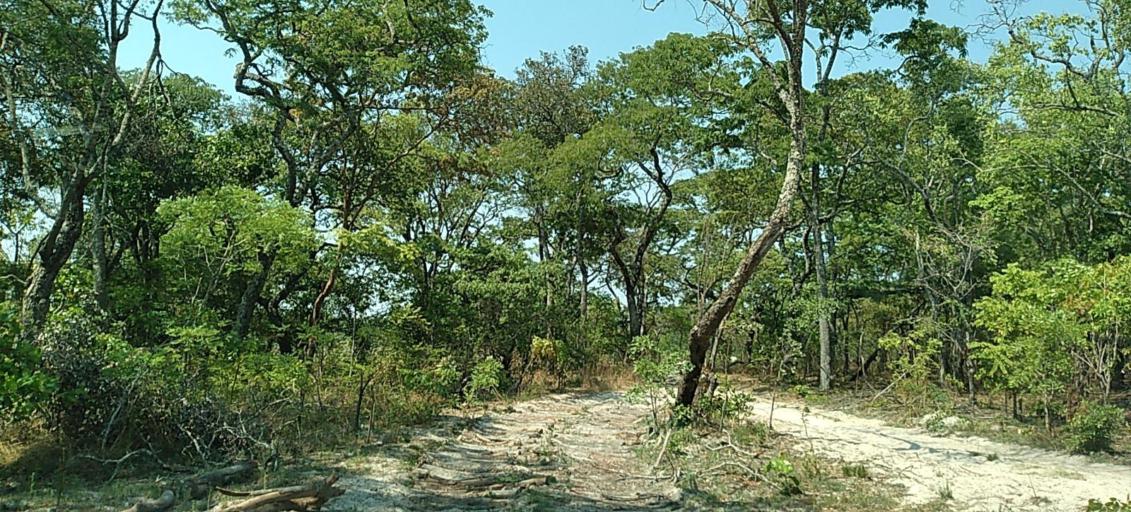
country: ZM
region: Copperbelt
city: Mpongwe
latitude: -13.7792
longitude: 28.1074
